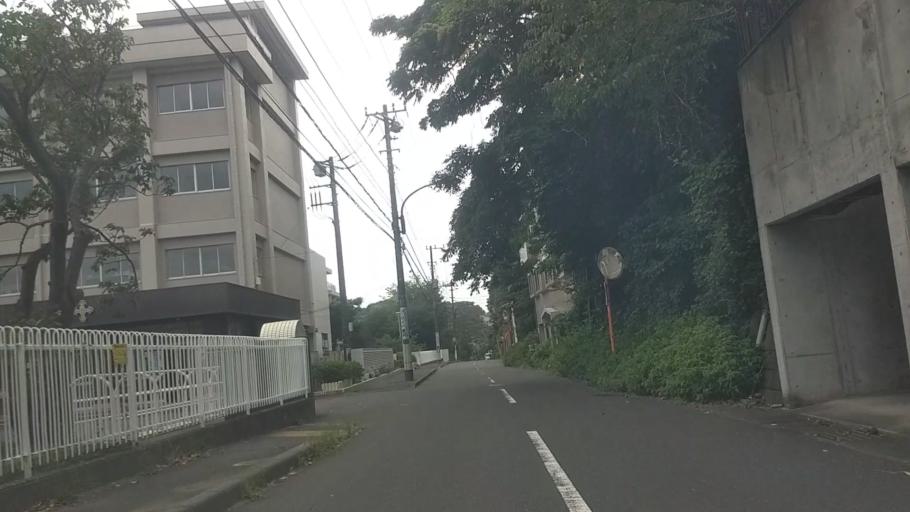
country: JP
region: Kanagawa
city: Yokosuka
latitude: 35.2532
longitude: 139.7331
